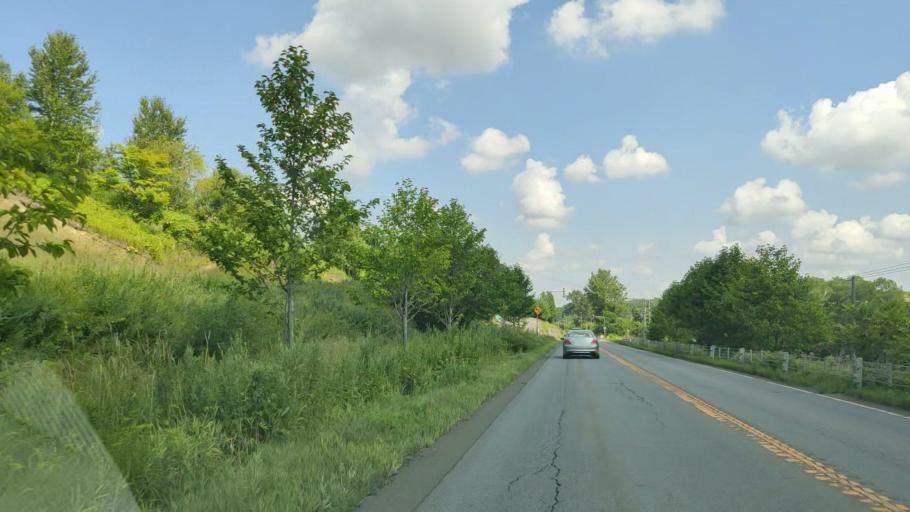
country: JP
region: Hokkaido
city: Shimo-furano
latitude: 43.5582
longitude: 142.4348
